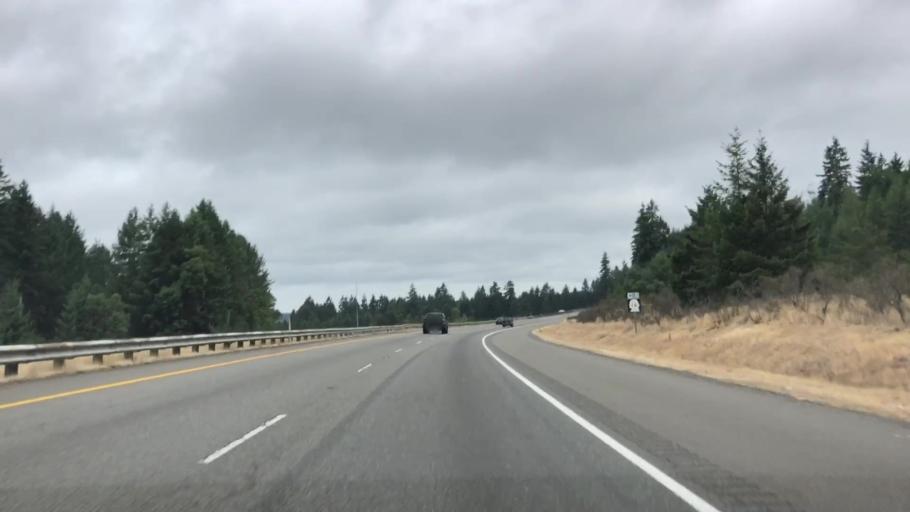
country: US
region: Washington
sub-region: Pierce County
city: Purdy
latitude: 47.3688
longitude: -122.6189
